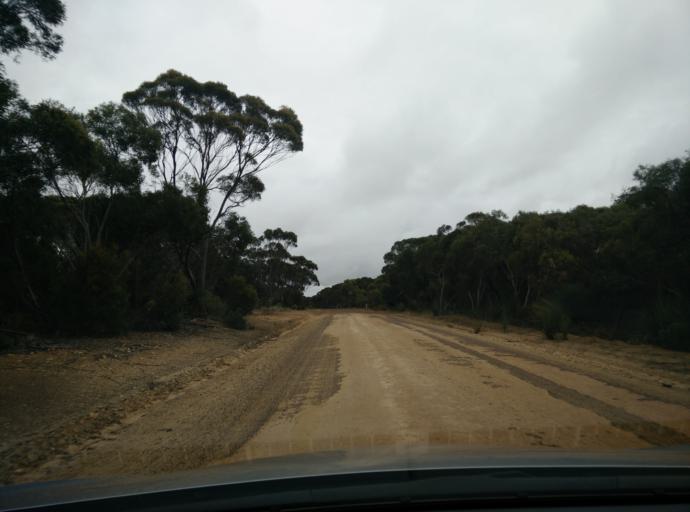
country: AU
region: South Australia
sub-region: Kangaroo Island
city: Kingscote
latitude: -35.8546
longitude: 137.4720
